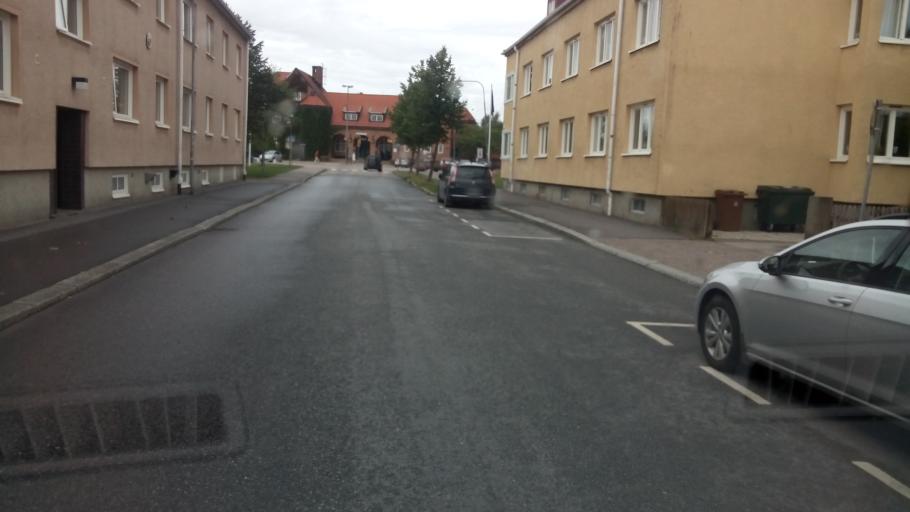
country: SE
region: Soedermanland
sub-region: Nykopings Kommun
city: Nykoping
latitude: 58.7554
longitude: 16.9956
